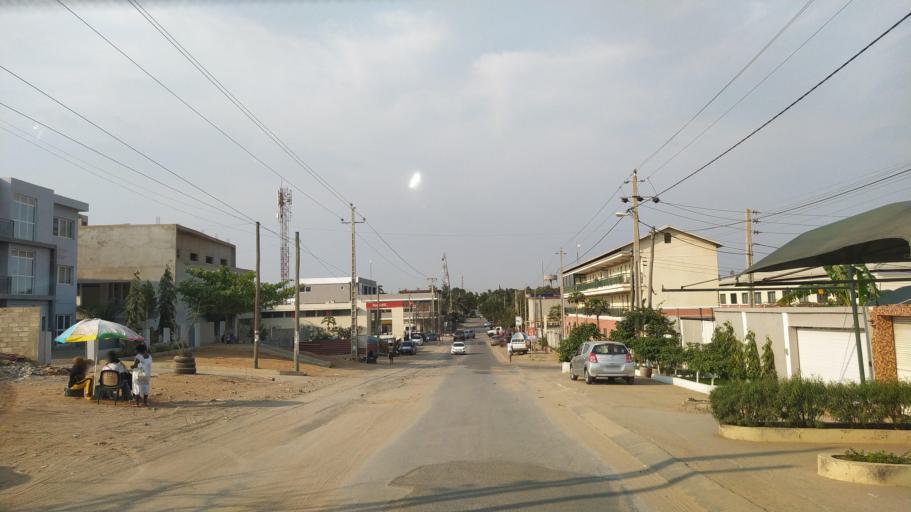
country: AO
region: Luanda
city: Luanda
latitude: -8.9118
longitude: 13.2254
